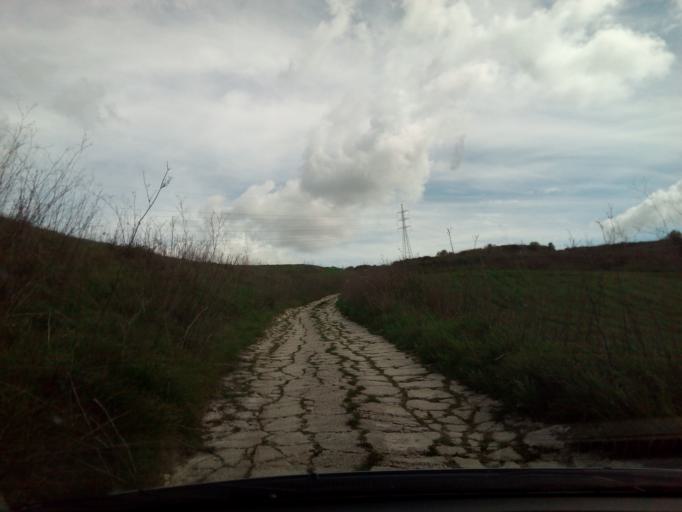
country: CY
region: Pafos
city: Tala
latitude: 34.8993
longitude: 32.4915
